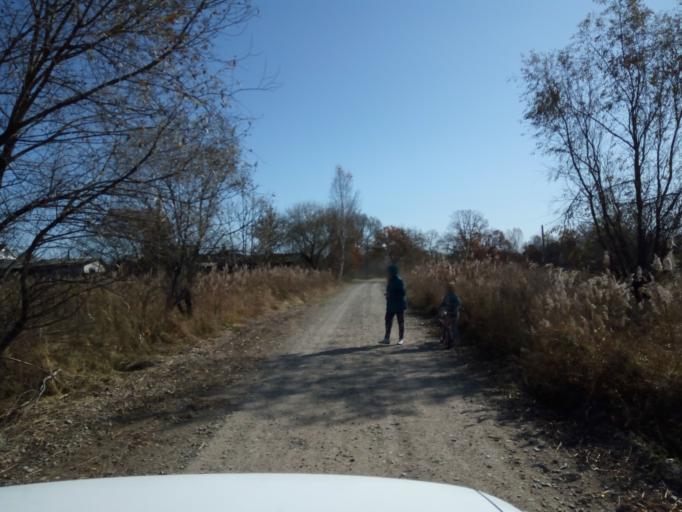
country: RU
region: Primorskiy
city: Dal'nerechensk
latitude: 45.9215
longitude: 133.7829
